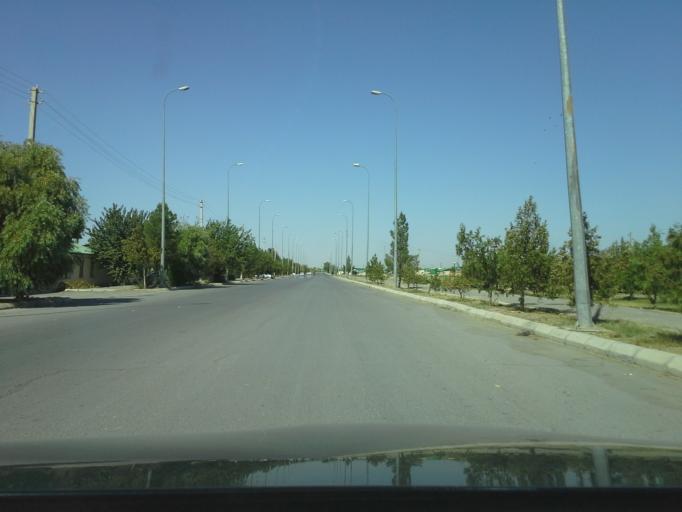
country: TM
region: Ahal
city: Ashgabat
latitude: 38.0051
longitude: 58.3044
